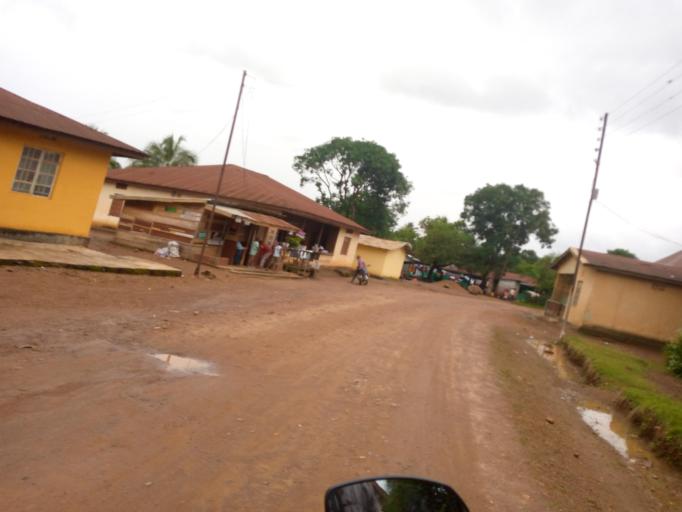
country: SL
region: Eastern Province
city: Kenema
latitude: 7.8840
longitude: -11.1784
